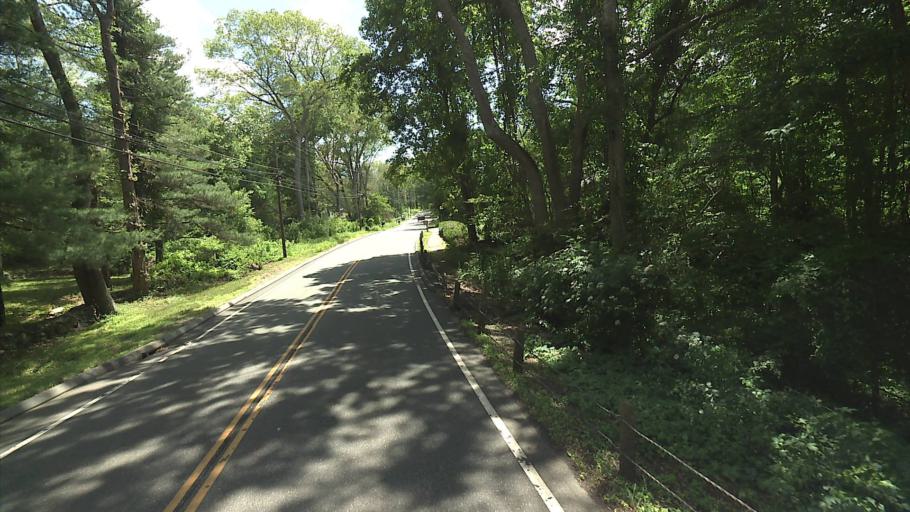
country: US
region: Connecticut
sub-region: New London County
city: Old Mystic
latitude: 41.3856
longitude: -71.9790
